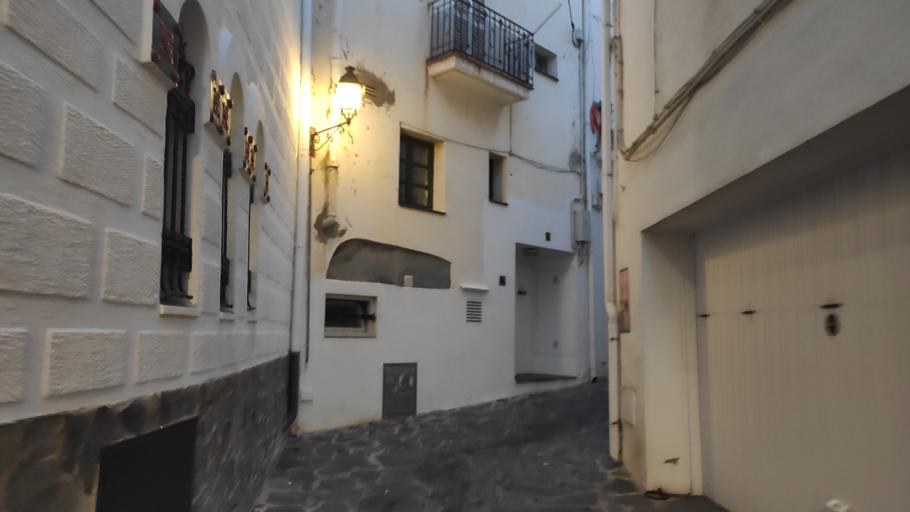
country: ES
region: Catalonia
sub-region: Provincia de Girona
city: Cadaques
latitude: 42.2889
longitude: 3.2806
